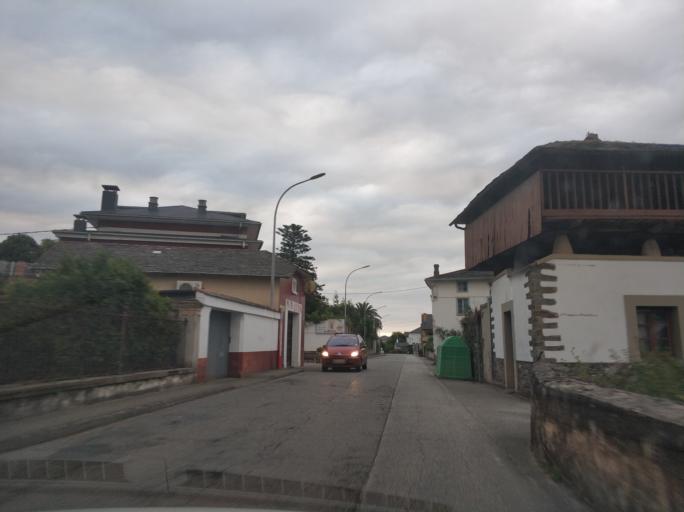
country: ES
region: Asturias
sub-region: Province of Asturias
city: Navia
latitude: 43.5438
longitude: -6.5272
